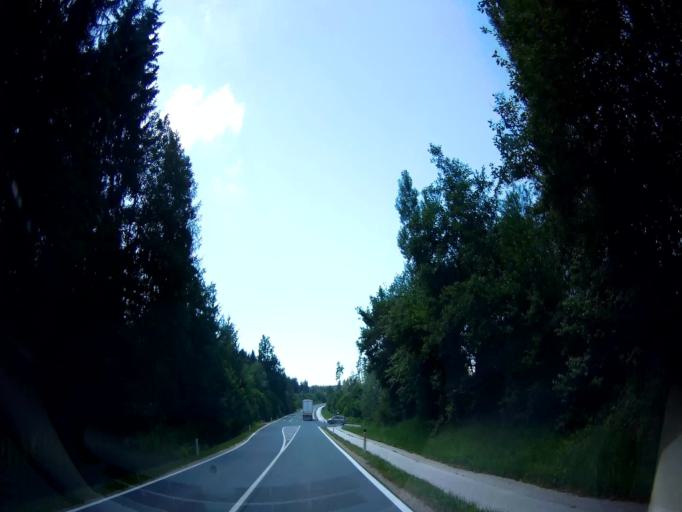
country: AT
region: Carinthia
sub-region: Politischer Bezirk Volkermarkt
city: Eberndorf
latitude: 46.6095
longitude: 14.6851
